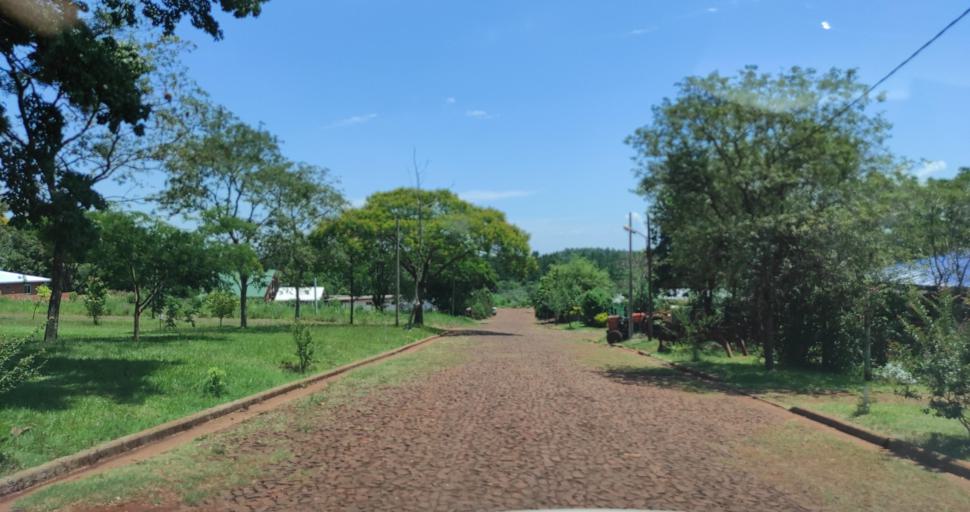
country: AR
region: Misiones
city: Ruiz de Montoya
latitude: -26.9704
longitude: -55.0486
